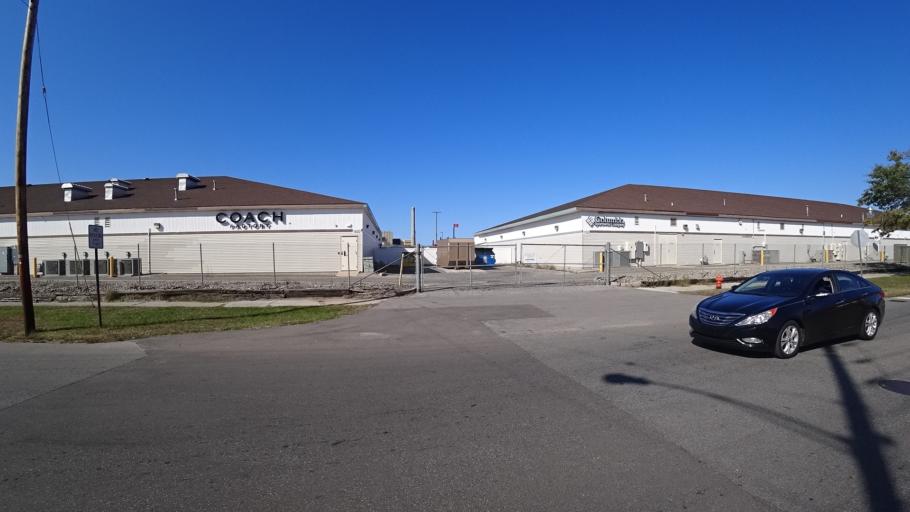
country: US
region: Indiana
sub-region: LaPorte County
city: Michigan City
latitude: 41.7124
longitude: -86.9054
